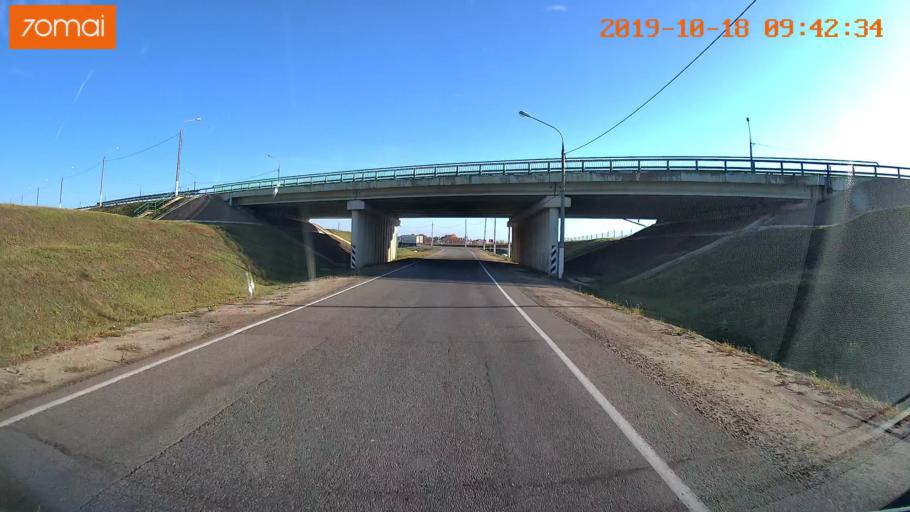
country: RU
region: Tula
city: Kazachka
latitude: 53.2881
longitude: 38.1781
